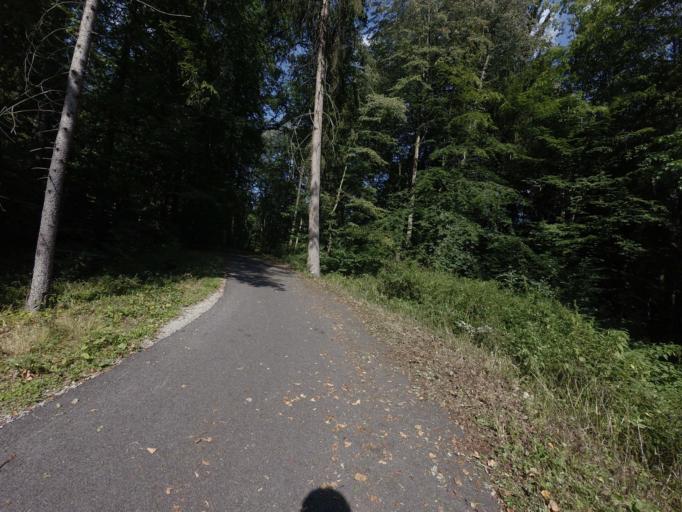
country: CZ
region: Jihocesky
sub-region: Okres Ceske Budejovice
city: Hluboka nad Vltavou
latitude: 49.0849
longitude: 14.4669
